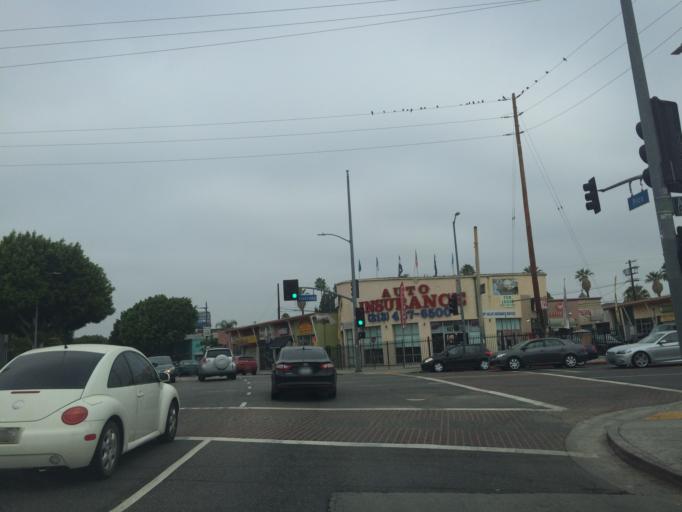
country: US
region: California
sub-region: Los Angeles County
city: Echo Park
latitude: 34.0471
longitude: -118.2823
